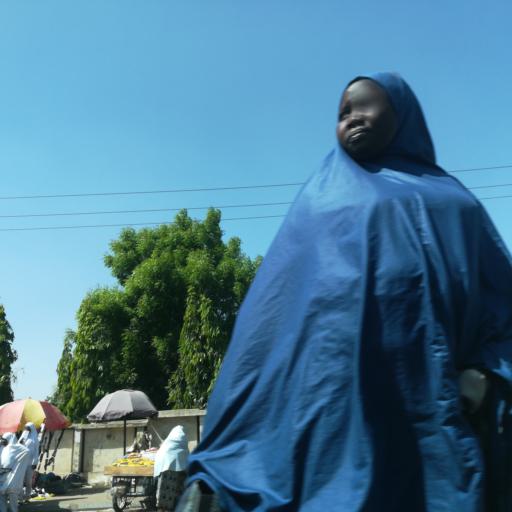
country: NG
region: Kano
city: Kano
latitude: 11.9989
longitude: 8.5233
